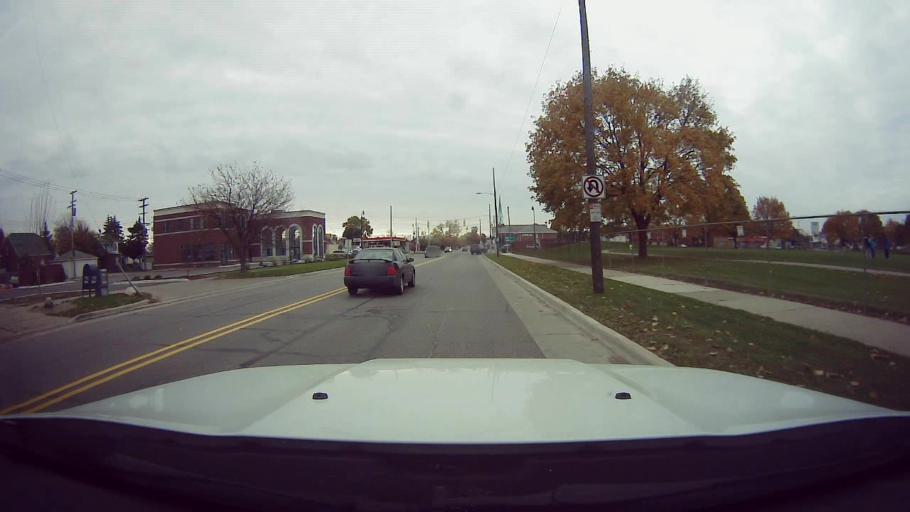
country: US
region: Michigan
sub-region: Wayne County
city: Dearborn
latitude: 42.3303
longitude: -83.1860
